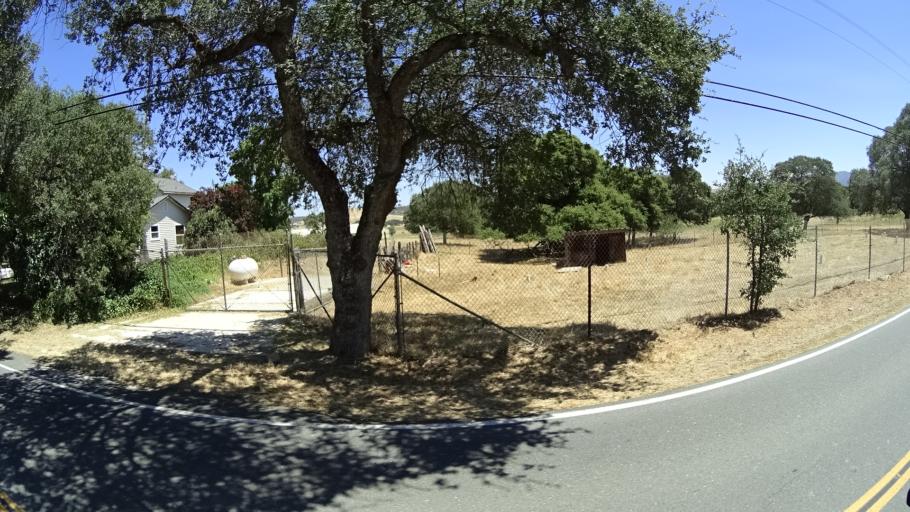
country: US
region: California
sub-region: Calaveras County
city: Valley Springs
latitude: 38.2098
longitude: -120.8302
